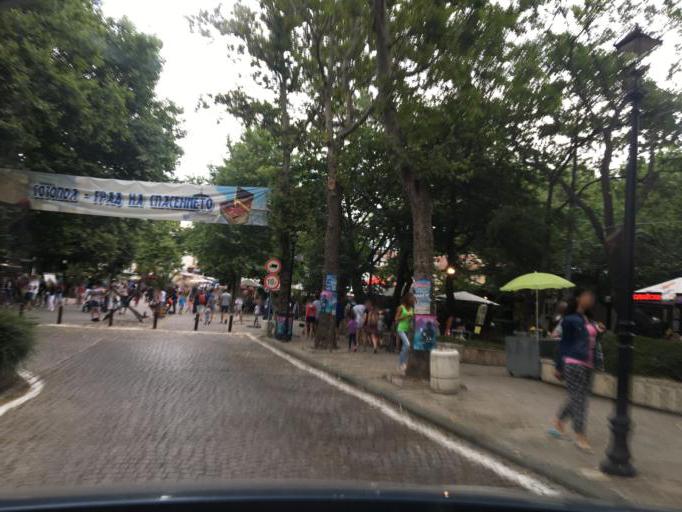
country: BG
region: Burgas
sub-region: Obshtina Sozopol
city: Sozopol
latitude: 42.4210
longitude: 27.6934
